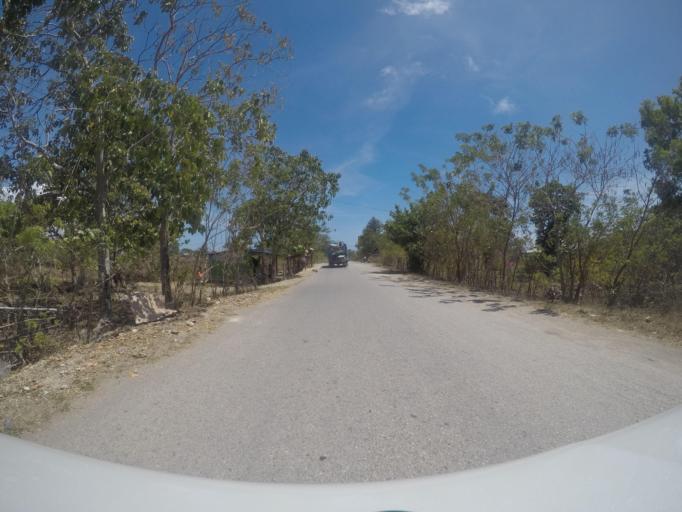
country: TL
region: Baucau
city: Baucau
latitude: -8.4638
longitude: 126.4293
